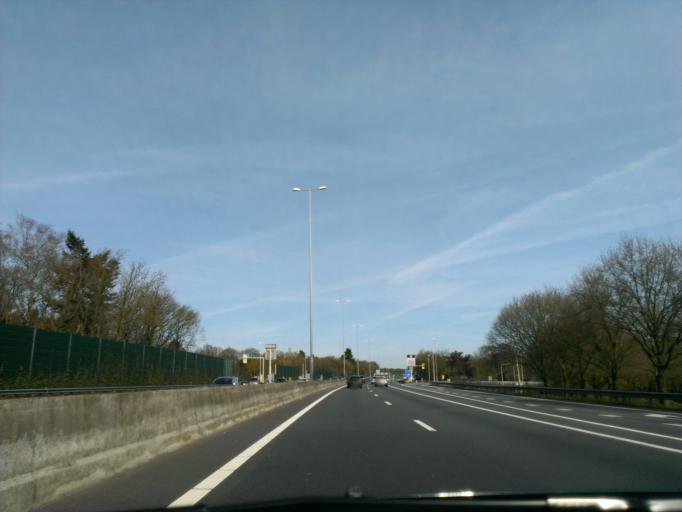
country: NL
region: North Holland
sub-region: Gemeente Laren
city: Laren
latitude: 52.2478
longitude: 5.2145
